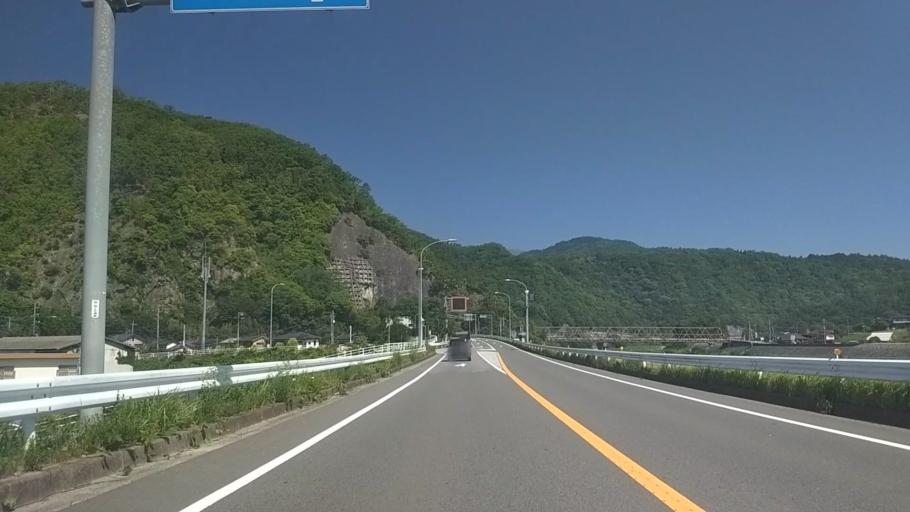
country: JP
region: Yamanashi
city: Ryuo
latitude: 35.4924
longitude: 138.4518
